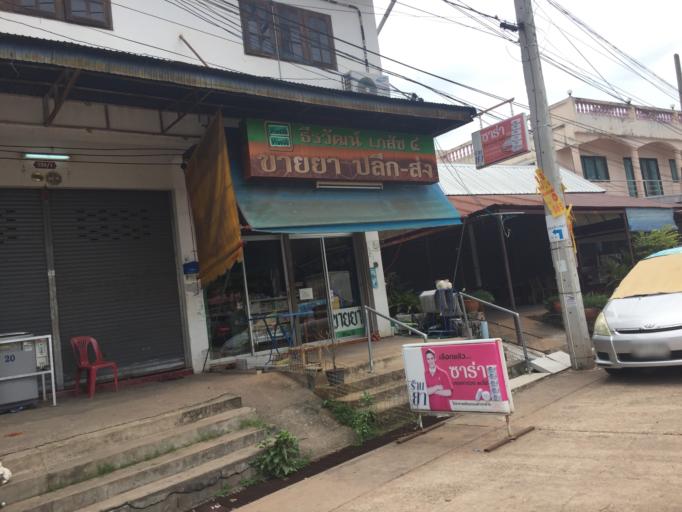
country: TH
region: Changwat Udon Thani
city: Nong Saeng
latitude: 17.2797
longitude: 102.8700
